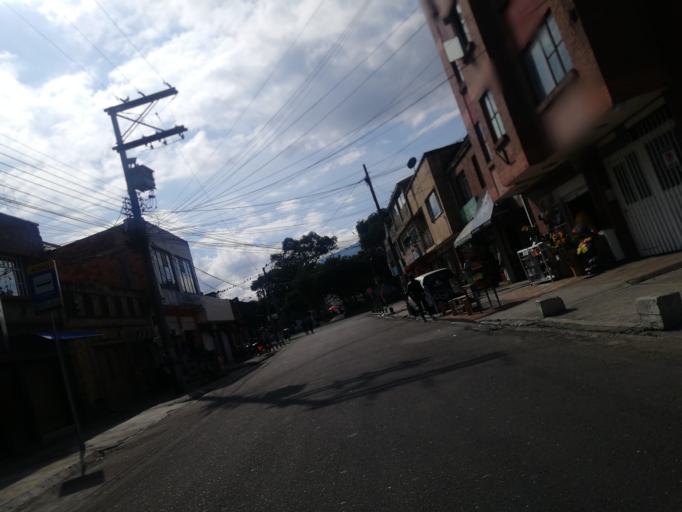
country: CO
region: Bogota D.C.
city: Bogota
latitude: 4.5908
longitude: -74.1053
